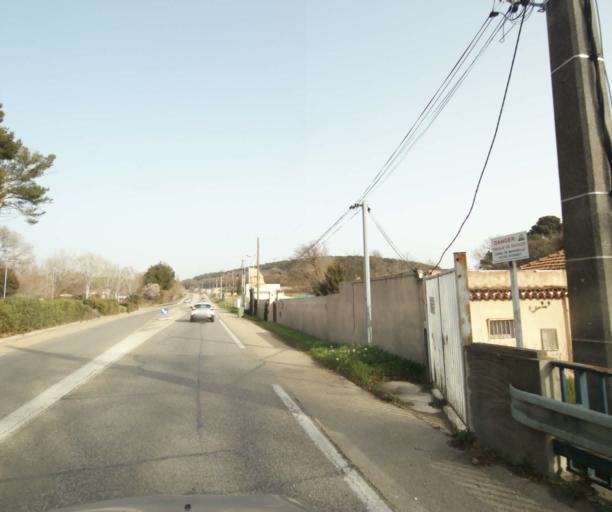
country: FR
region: Provence-Alpes-Cote d'Azur
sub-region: Departement des Bouches-du-Rhone
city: Les Pennes-Mirabeau
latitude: 43.4110
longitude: 5.3279
